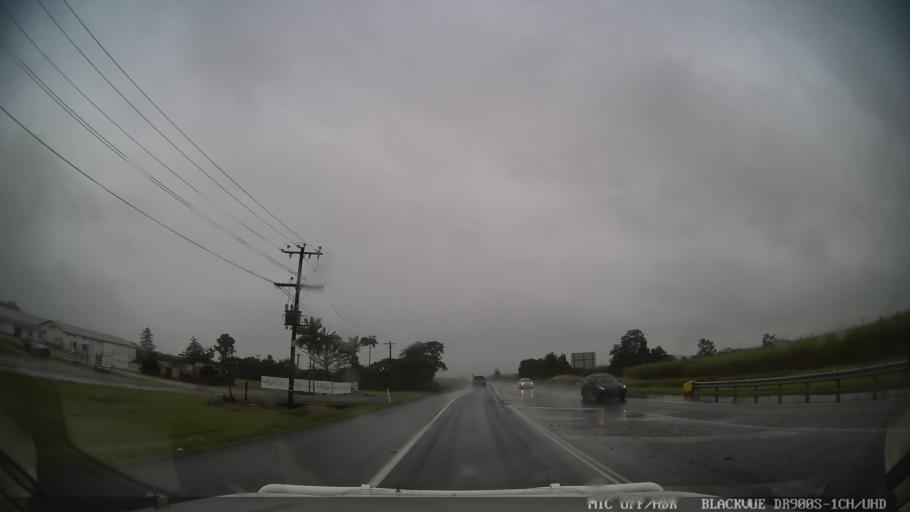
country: AU
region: Queensland
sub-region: Cassowary Coast
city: Innisfail
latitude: -17.7470
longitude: 146.0284
